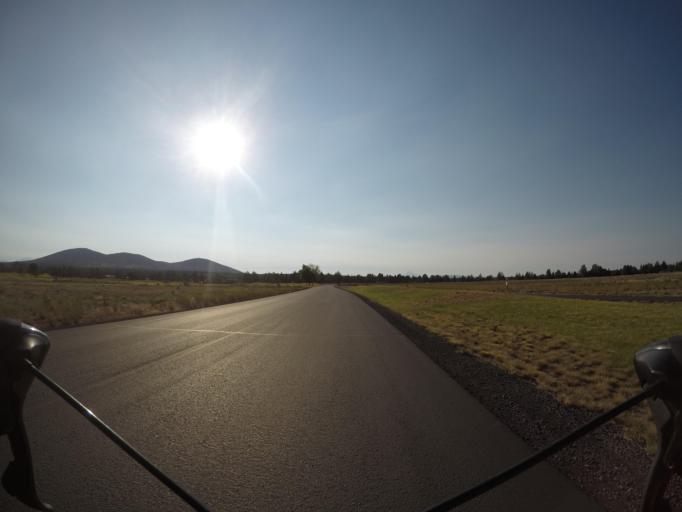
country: US
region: Oregon
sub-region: Deschutes County
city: Redmond
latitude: 44.2621
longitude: -121.2526
